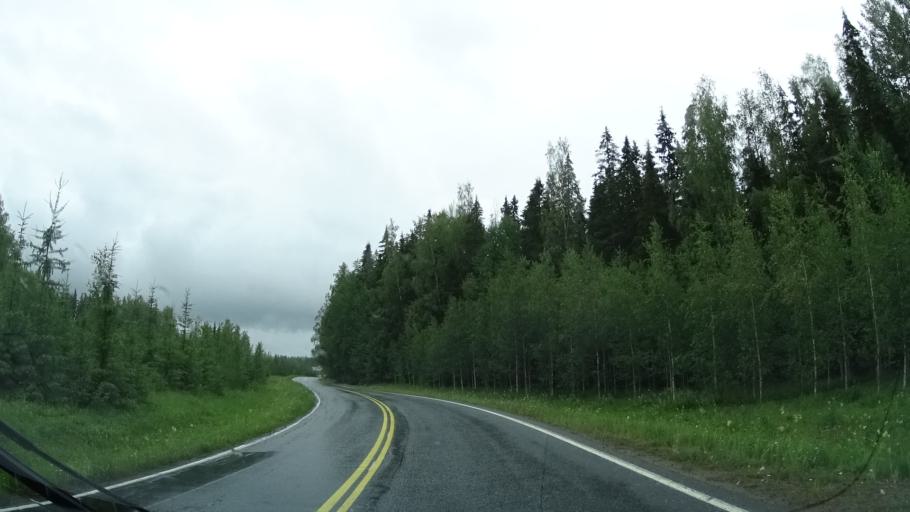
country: FI
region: Haeme
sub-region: Forssa
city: Humppila
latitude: 60.9920
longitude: 23.2569
